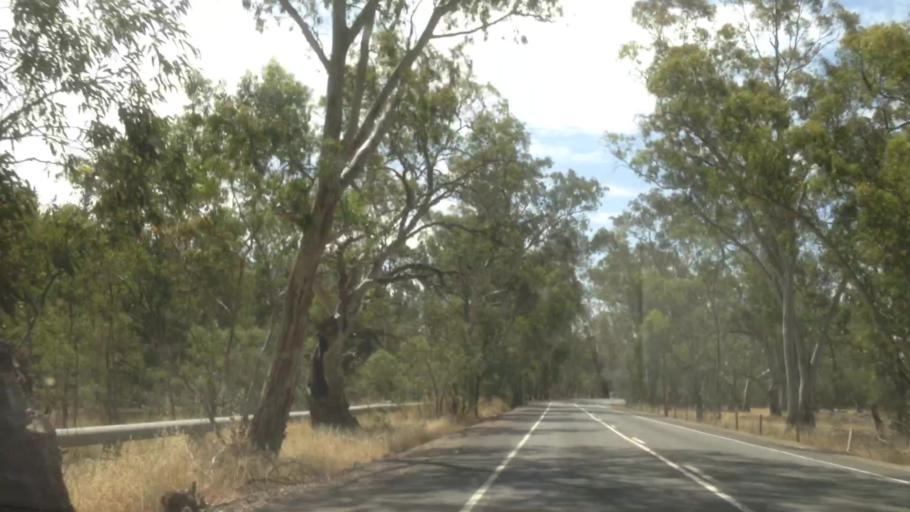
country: AU
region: South Australia
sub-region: Adelaide Hills
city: Birdwood
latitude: -34.7444
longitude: 138.9627
